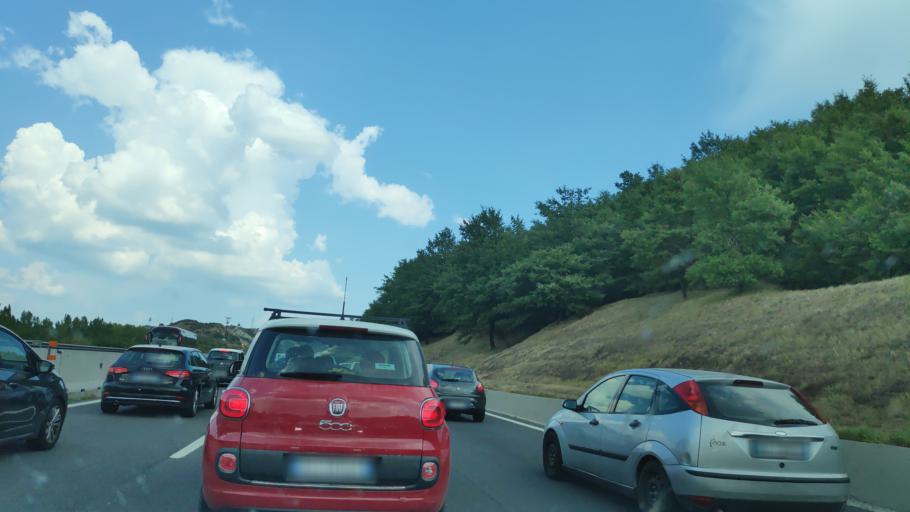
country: IT
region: Umbria
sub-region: Provincia di Terni
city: Ficulle
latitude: 42.8247
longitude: 12.0409
